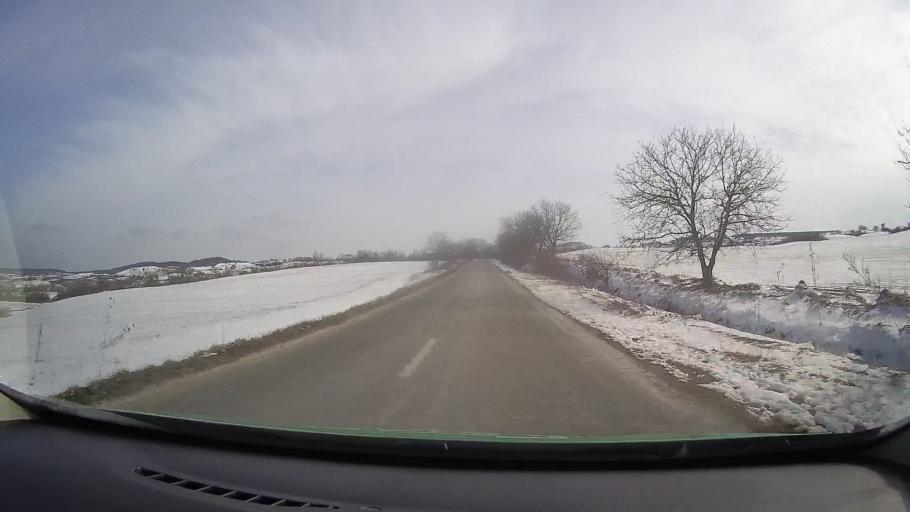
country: RO
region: Mures
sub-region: Comuna Apold
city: Apold
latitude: 46.1159
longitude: 24.8259
